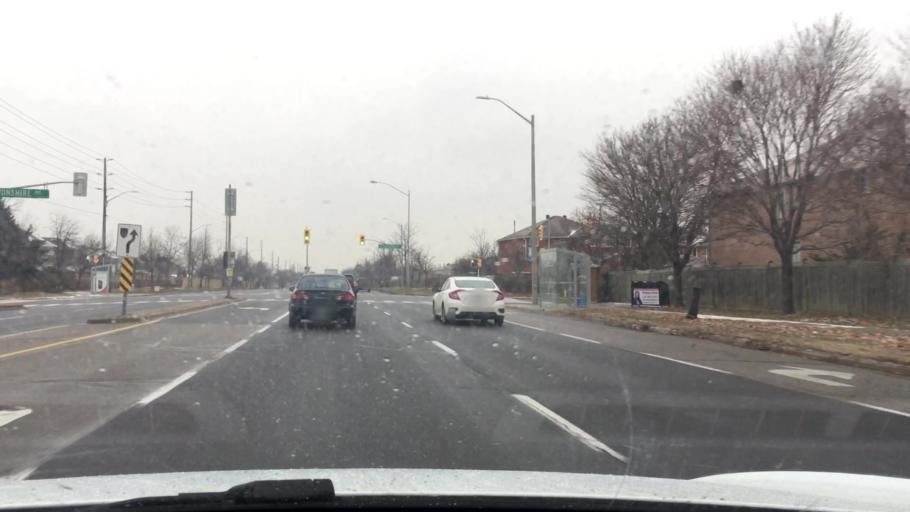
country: CA
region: Ontario
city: Markham
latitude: 43.8379
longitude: -79.2769
